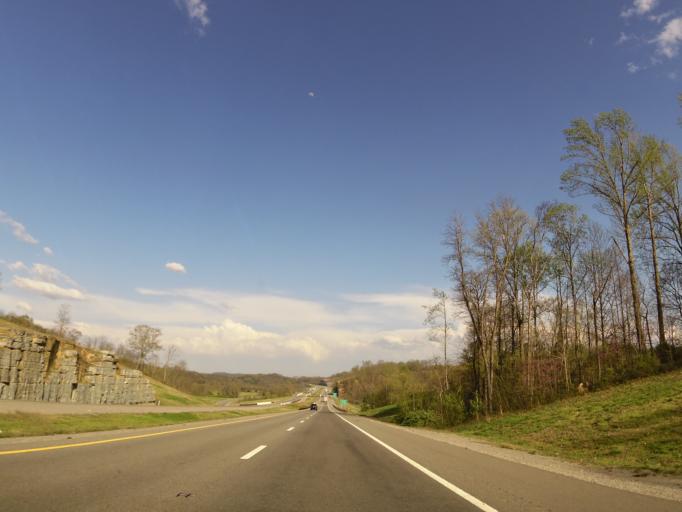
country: US
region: Tennessee
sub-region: Williamson County
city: Thompson's Station
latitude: 35.8181
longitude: -87.0029
